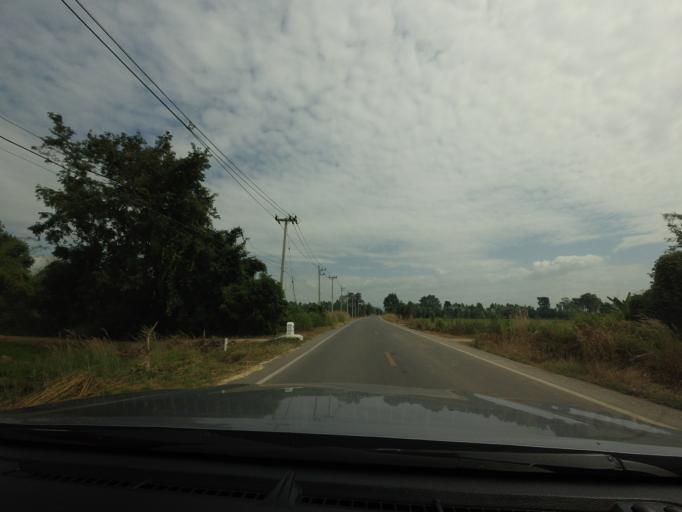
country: TH
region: Phitsanulok
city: Phitsanulok
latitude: 16.7208
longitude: 100.3341
